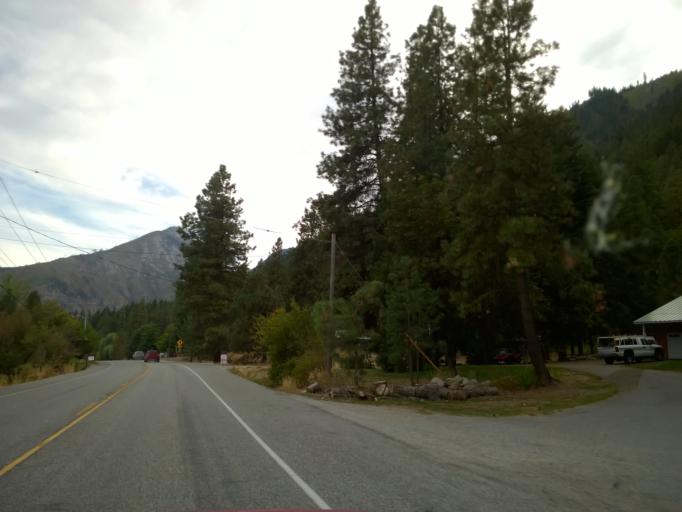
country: US
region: Washington
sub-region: Chelan County
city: Leavenworth
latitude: 47.5719
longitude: -120.6786
